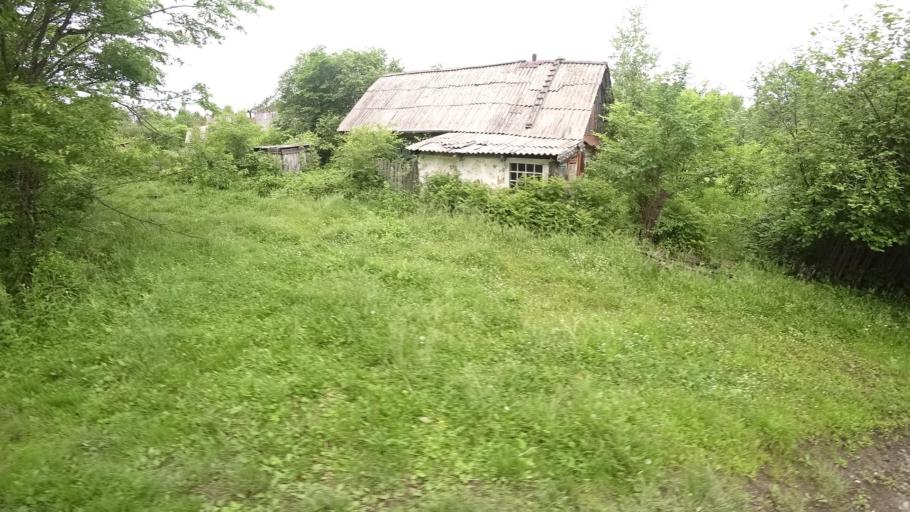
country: RU
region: Khabarovsk Krai
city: Amursk
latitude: 49.9053
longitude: 136.1324
